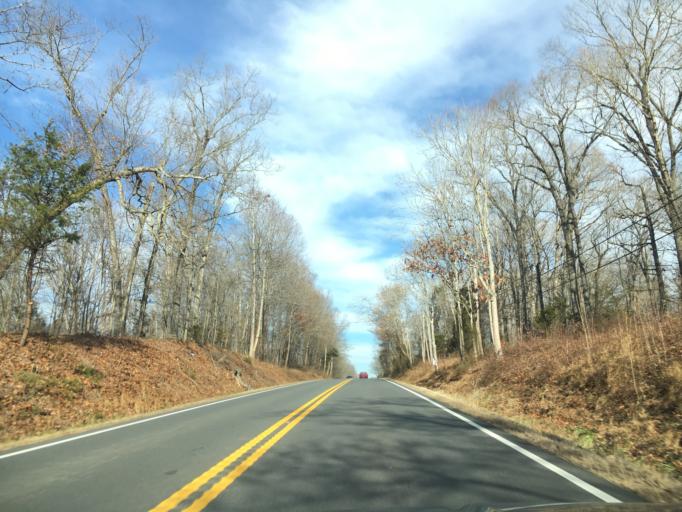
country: US
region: Virginia
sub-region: Fauquier County
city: Warrenton
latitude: 38.6339
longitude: -77.9344
